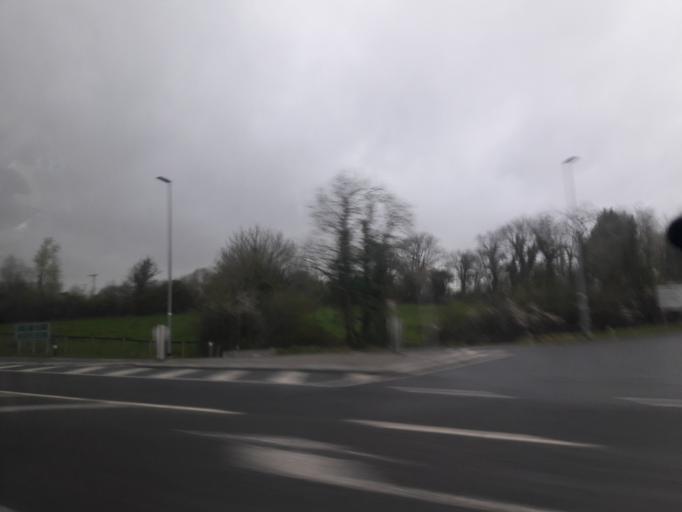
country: IE
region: Connaught
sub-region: County Leitrim
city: Carrick-on-Shannon
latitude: 53.9190
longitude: -7.9852
